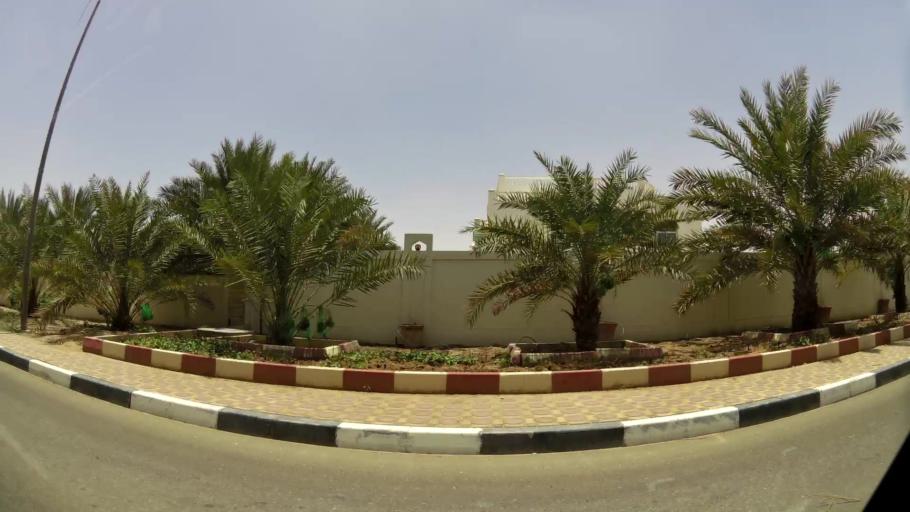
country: OM
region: Al Buraimi
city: Al Buraymi
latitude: 24.2616
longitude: 55.7117
